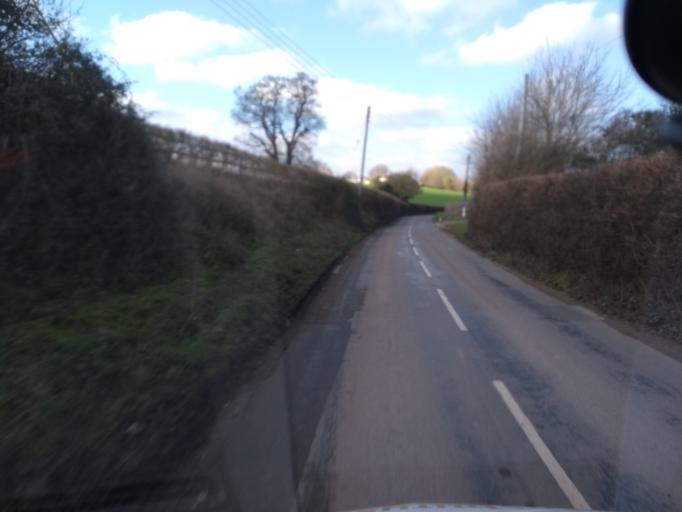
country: GB
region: England
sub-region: Somerset
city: Taunton
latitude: 50.9929
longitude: -3.0771
